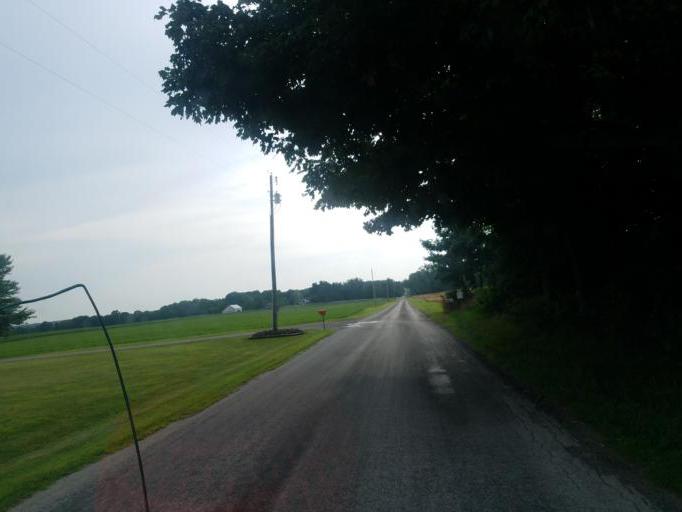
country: US
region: Ohio
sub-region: Wayne County
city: West Salem
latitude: 40.9009
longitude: -82.1272
